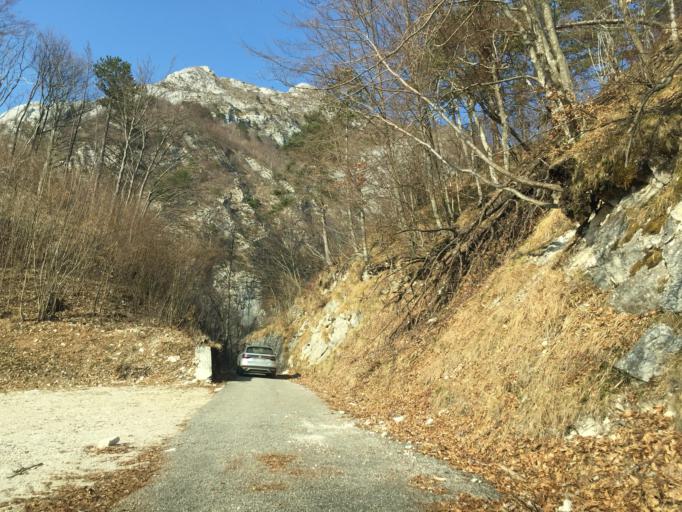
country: IT
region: Friuli Venezia Giulia
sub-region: Provincia di Udine
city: Amaro
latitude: 46.3893
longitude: 13.0720
